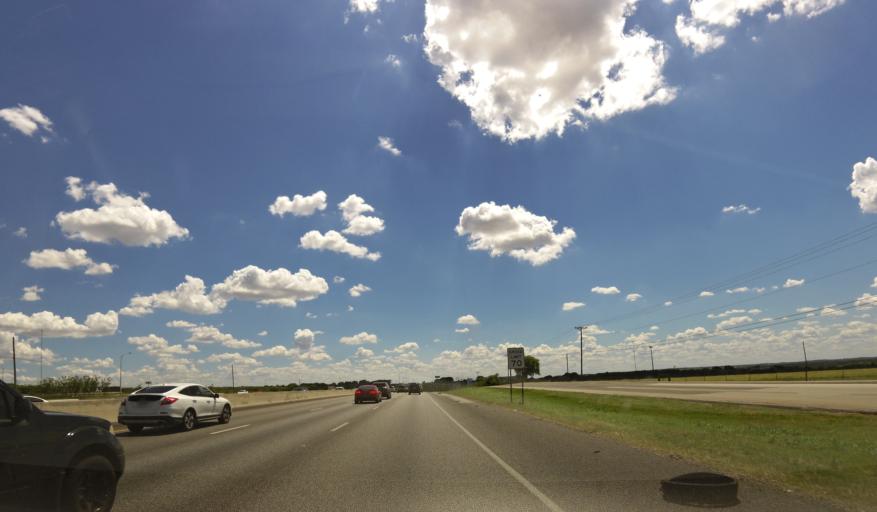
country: US
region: Texas
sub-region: Guadalupe County
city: Northcliff
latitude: 29.6371
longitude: -98.2172
